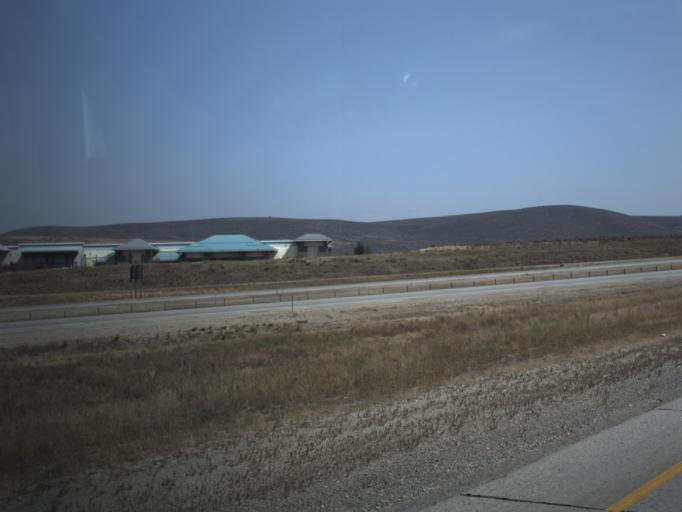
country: US
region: Utah
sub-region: Summit County
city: Snyderville
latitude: 40.7162
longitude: -111.4869
